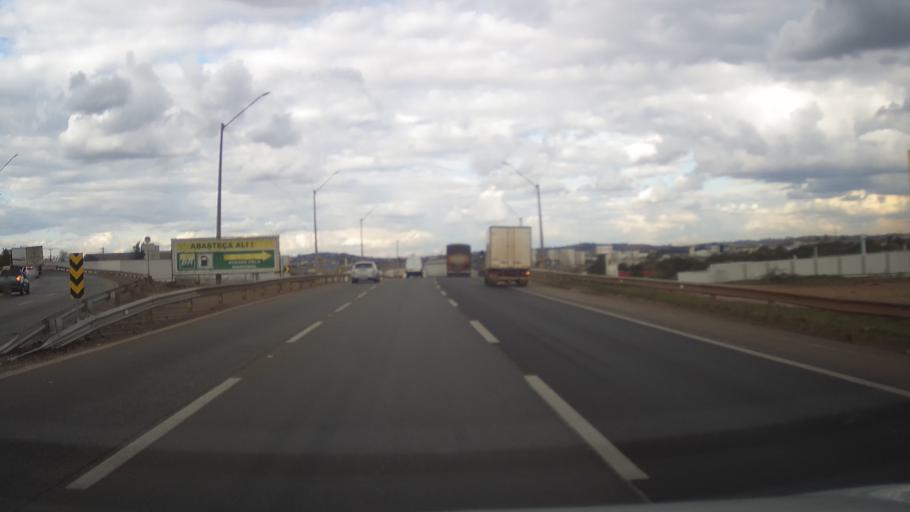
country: BR
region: Minas Gerais
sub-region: Betim
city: Betim
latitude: -19.9576
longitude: -44.1498
